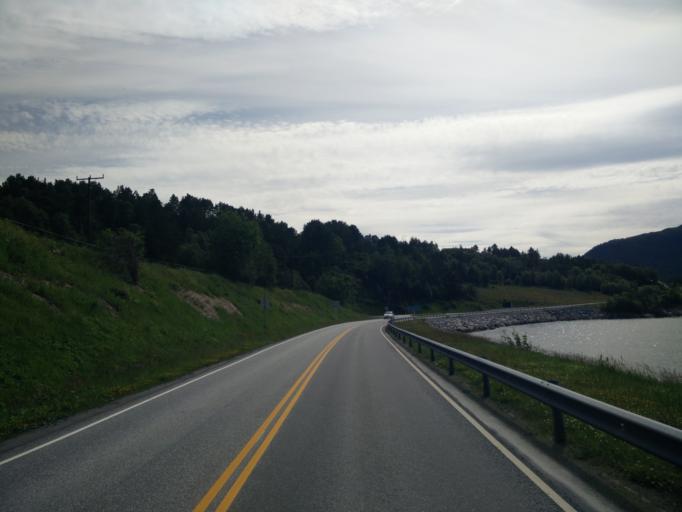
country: NO
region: More og Romsdal
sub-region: Kristiansund
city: Rensvik
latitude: 62.9798
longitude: 7.7945
